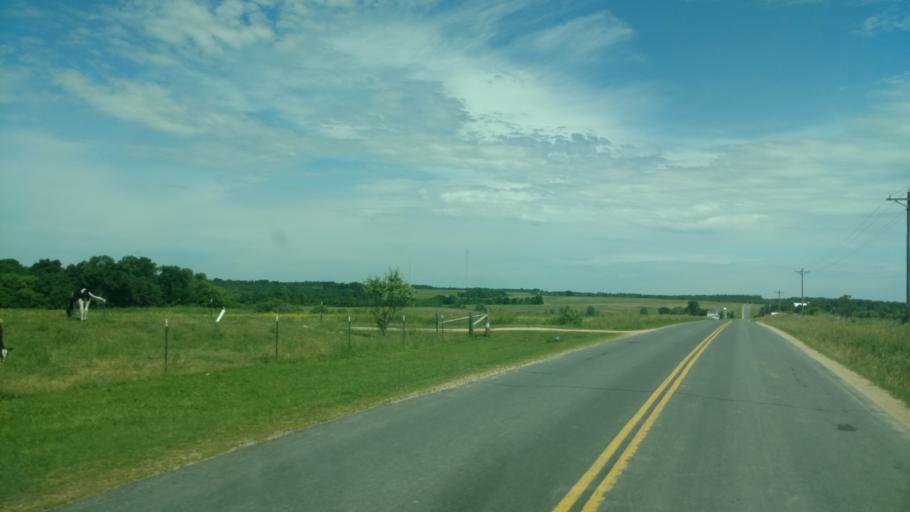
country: US
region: Wisconsin
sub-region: Vernon County
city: Hillsboro
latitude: 43.7605
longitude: -90.4330
